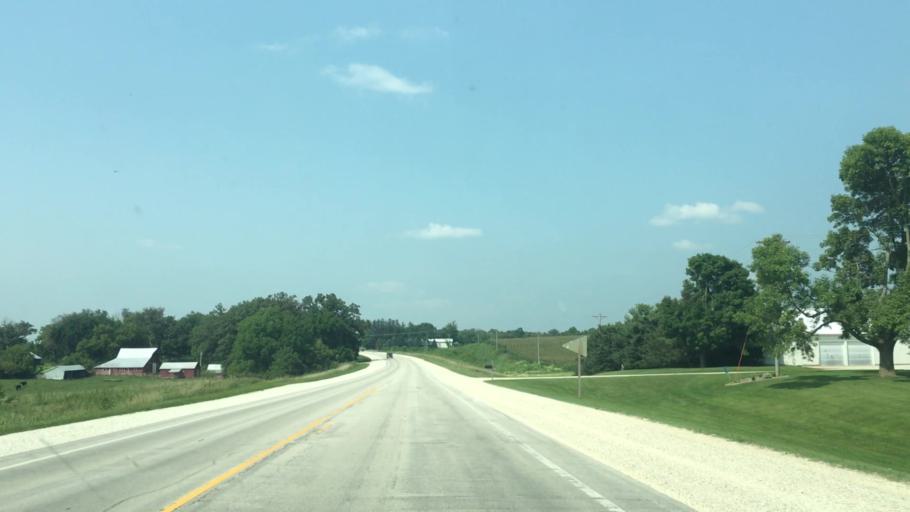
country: US
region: Iowa
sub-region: Winneshiek County
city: Decorah
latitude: 43.4242
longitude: -91.8593
